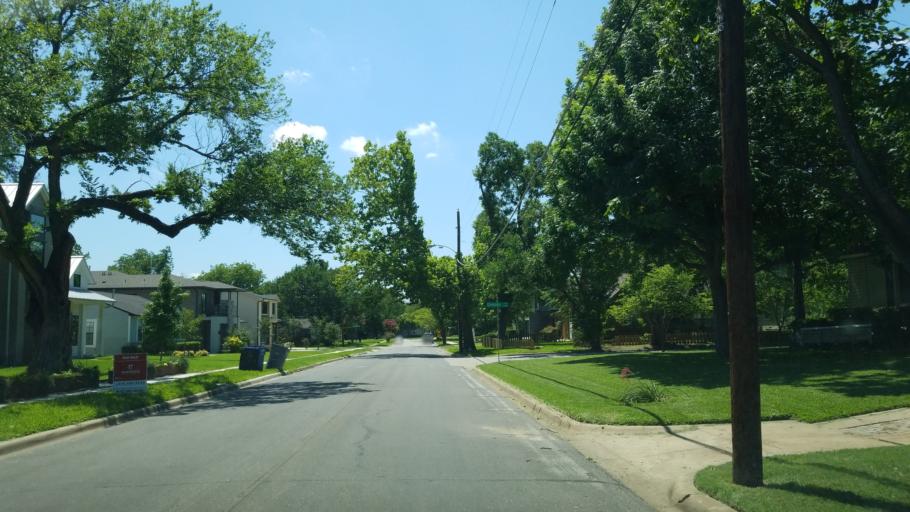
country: US
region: Texas
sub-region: Dallas County
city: University Park
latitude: 32.8771
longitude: -96.8491
